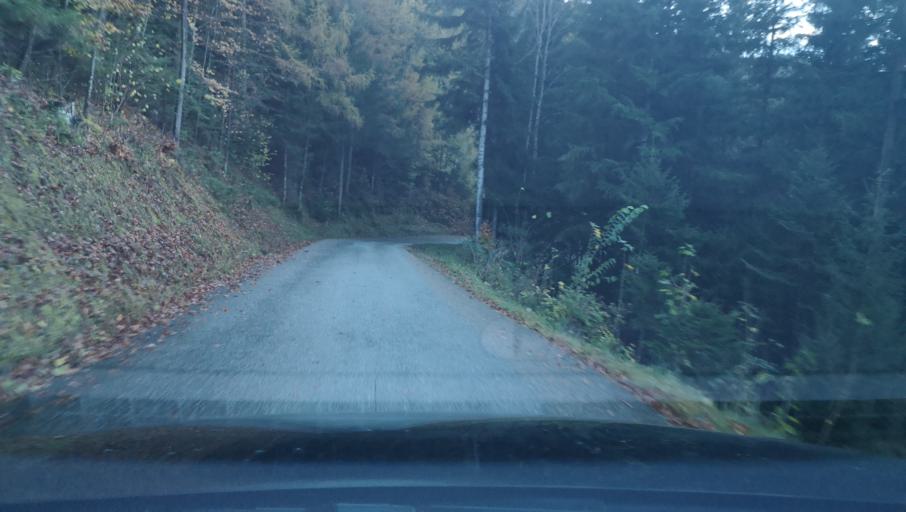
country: AT
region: Styria
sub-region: Politischer Bezirk Weiz
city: Birkfeld
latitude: 47.3350
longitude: 15.6687
